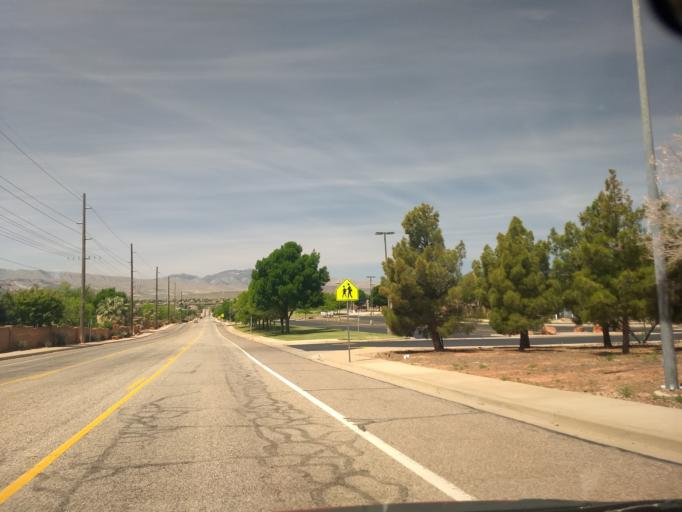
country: US
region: Utah
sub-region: Washington County
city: Santa Clara
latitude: 37.1431
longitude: -113.6249
